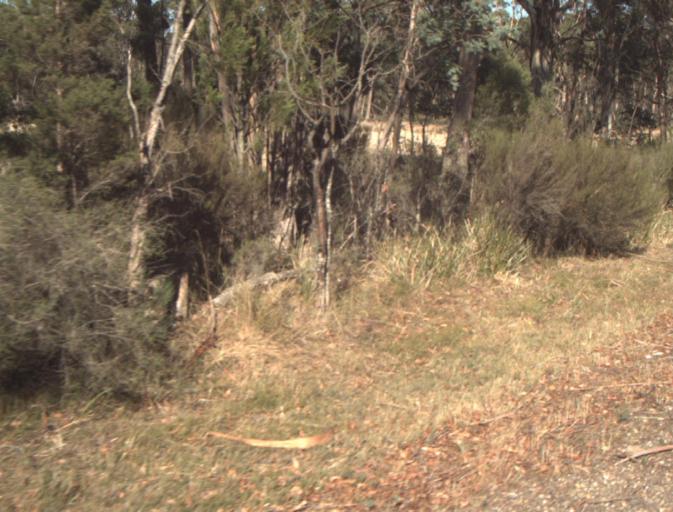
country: AU
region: Tasmania
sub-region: Launceston
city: Mayfield
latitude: -41.2945
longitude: 147.1317
